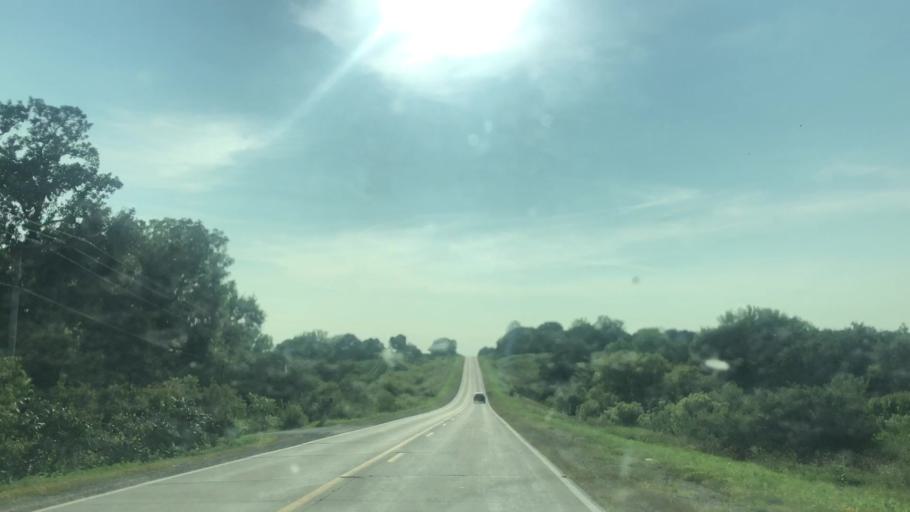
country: US
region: Iowa
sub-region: Marshall County
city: Marshalltown
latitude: 42.0490
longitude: -92.9778
